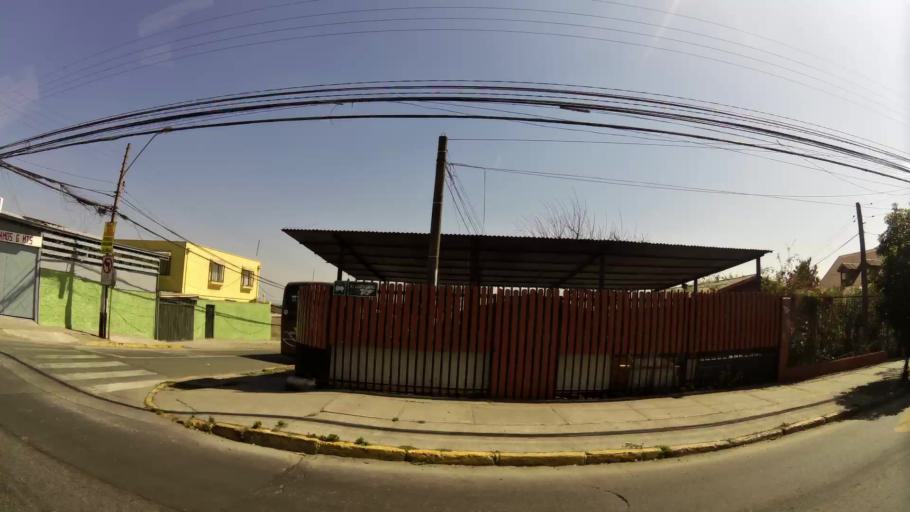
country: CL
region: Santiago Metropolitan
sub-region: Provincia de Santiago
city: Villa Presidente Frei, Nunoa, Santiago, Chile
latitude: -33.4702
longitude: -70.5412
